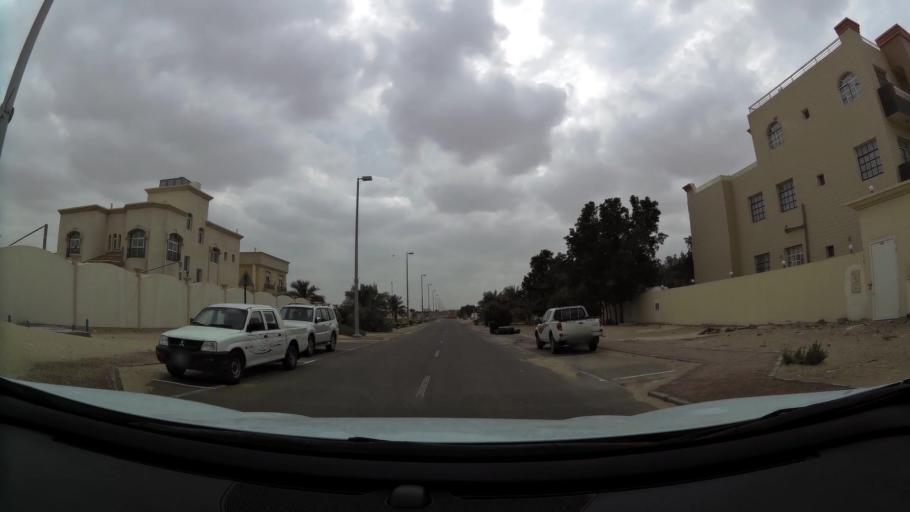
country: AE
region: Abu Dhabi
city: Abu Dhabi
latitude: 24.3815
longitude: 54.6360
